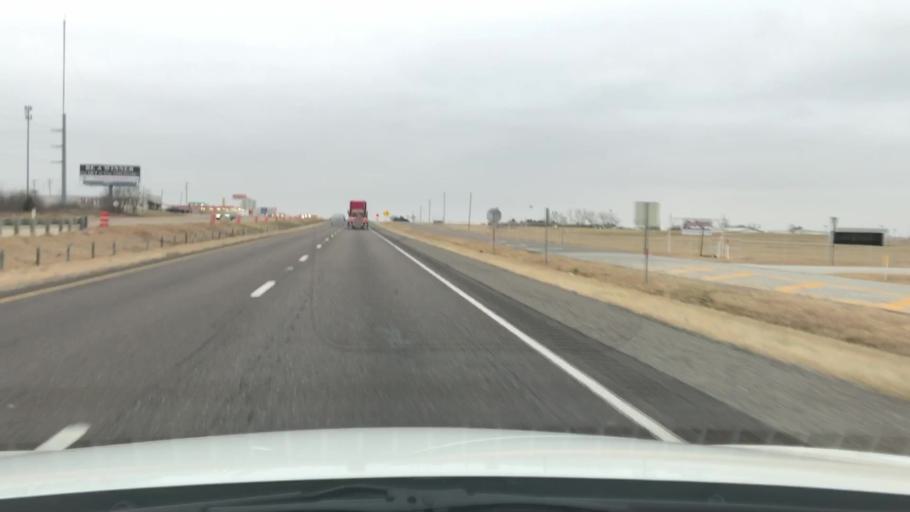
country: US
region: Texas
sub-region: Cooke County
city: Gainesville
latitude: 33.6816
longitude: -97.1561
